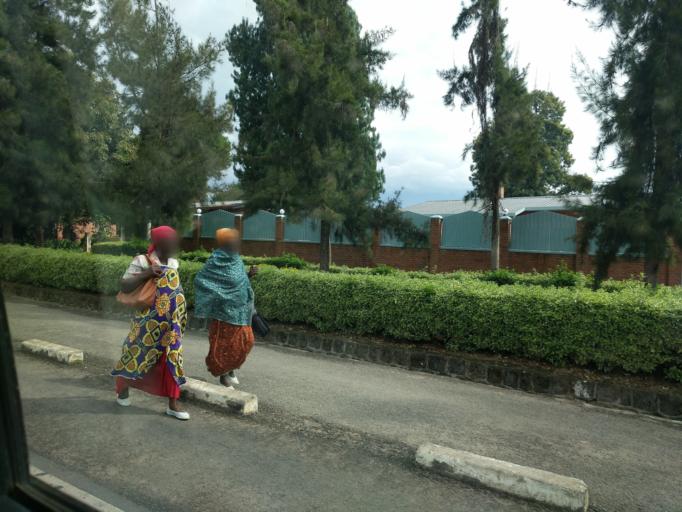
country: RW
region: Northern Province
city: Musanze
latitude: -1.4991
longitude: 29.6313
